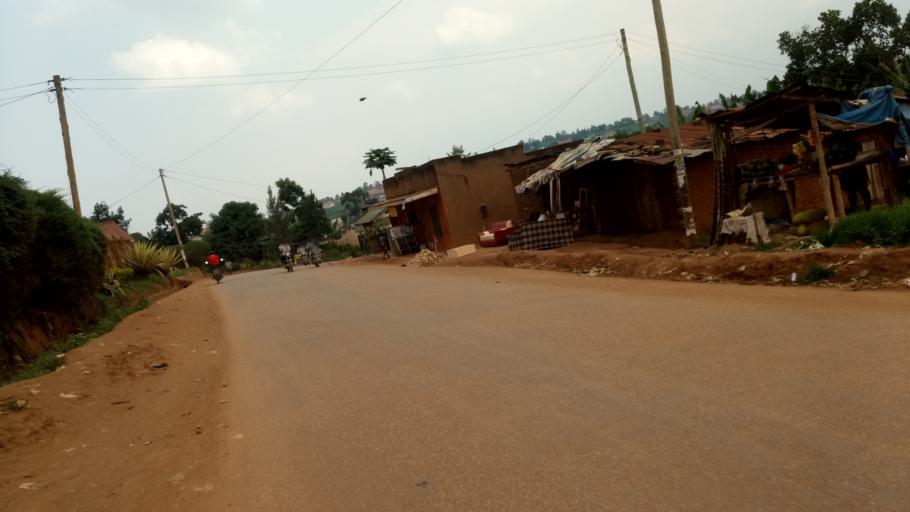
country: UG
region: Western Region
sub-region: Mbarara District
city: Mbarara
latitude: -0.6136
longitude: 30.6663
